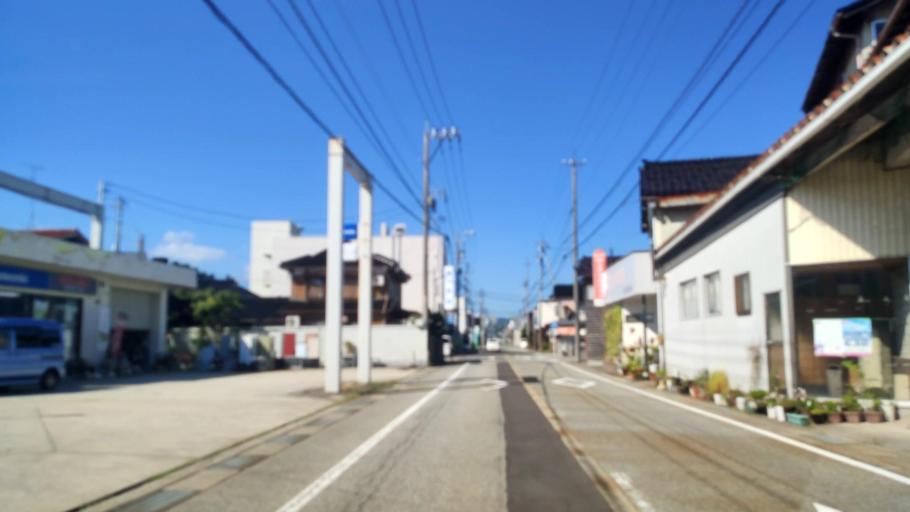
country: JP
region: Ishikawa
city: Nanao
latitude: 37.4382
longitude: 137.2653
